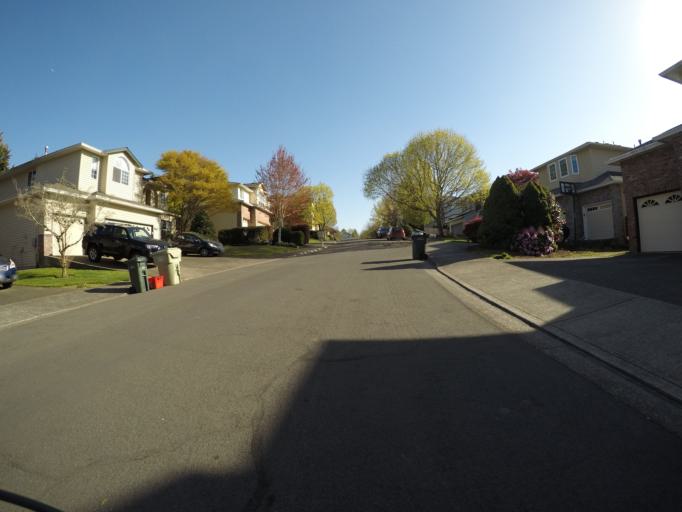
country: US
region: Oregon
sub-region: Washington County
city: Oak Hills
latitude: 45.5478
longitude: -122.8252
